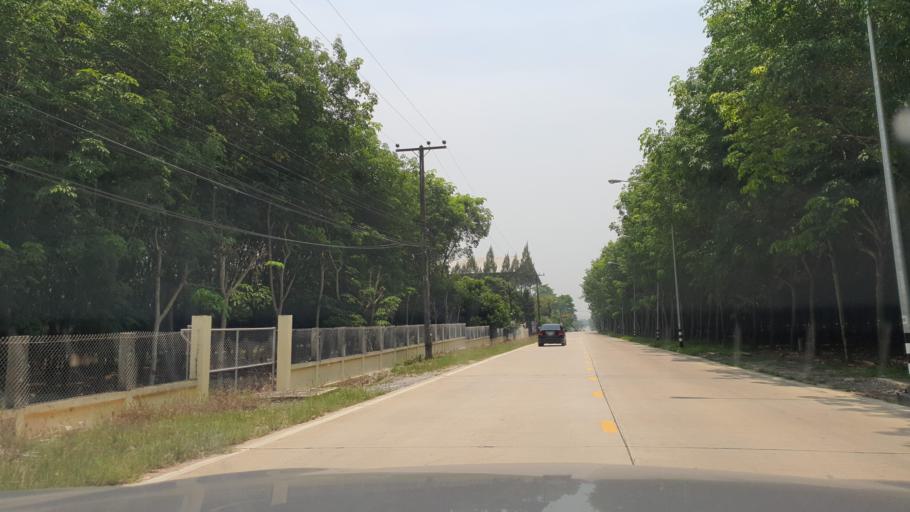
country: TH
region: Rayong
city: Nikhom Phattana
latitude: 12.7898
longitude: 101.1597
